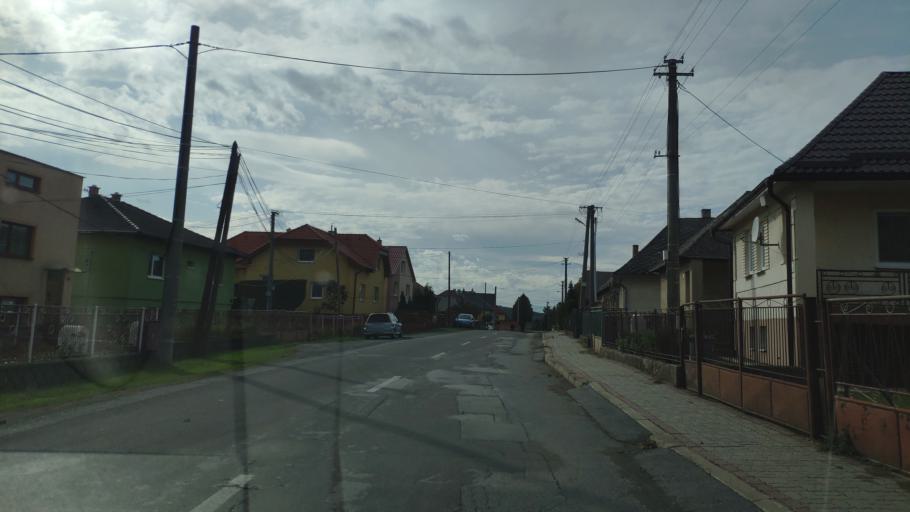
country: SK
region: Presovsky
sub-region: Okres Presov
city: Presov
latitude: 48.9457
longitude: 21.3381
